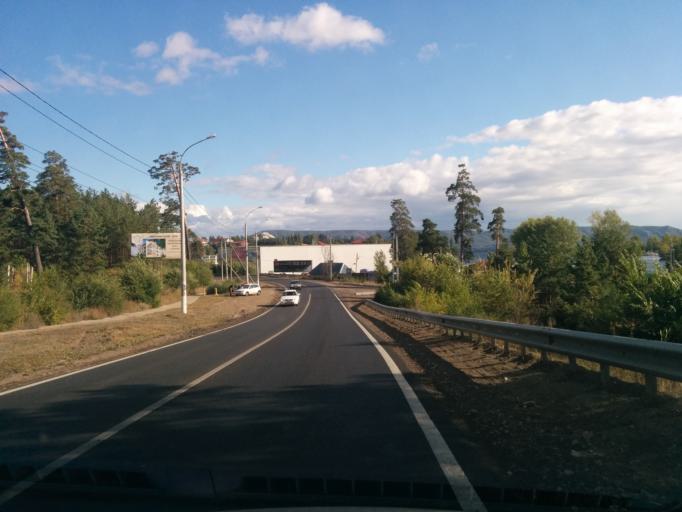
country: RU
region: Samara
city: Tol'yatti
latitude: 53.4783
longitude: 49.3229
